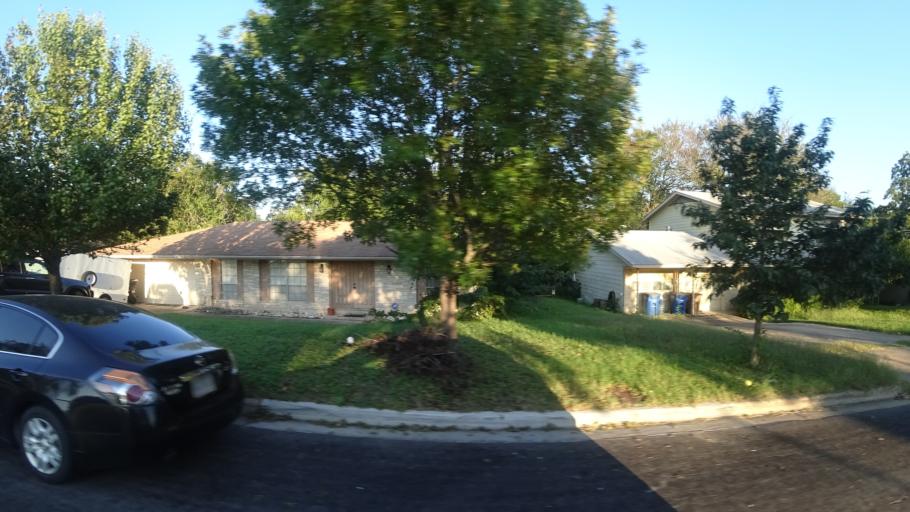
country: US
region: Texas
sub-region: Travis County
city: Wells Branch
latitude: 30.3676
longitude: -97.6731
